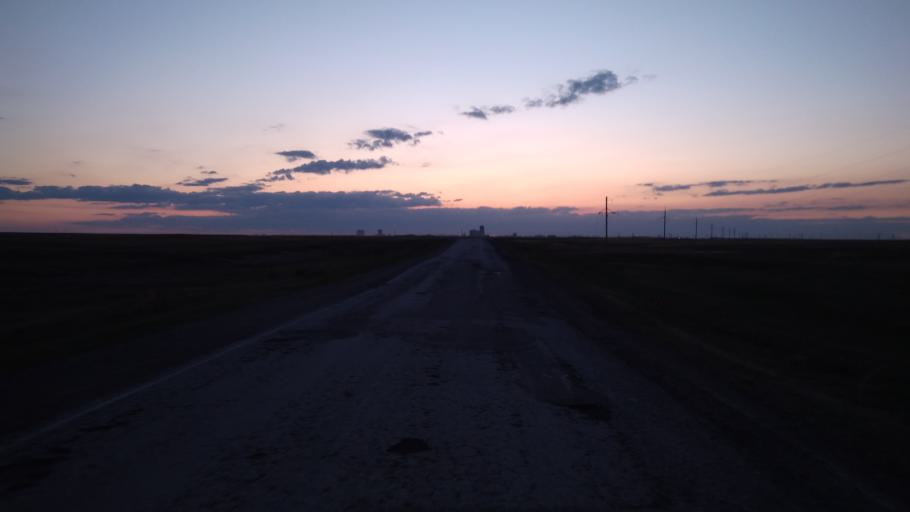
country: RU
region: Chelyabinsk
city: Troitsk
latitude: 54.0922
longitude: 61.6407
